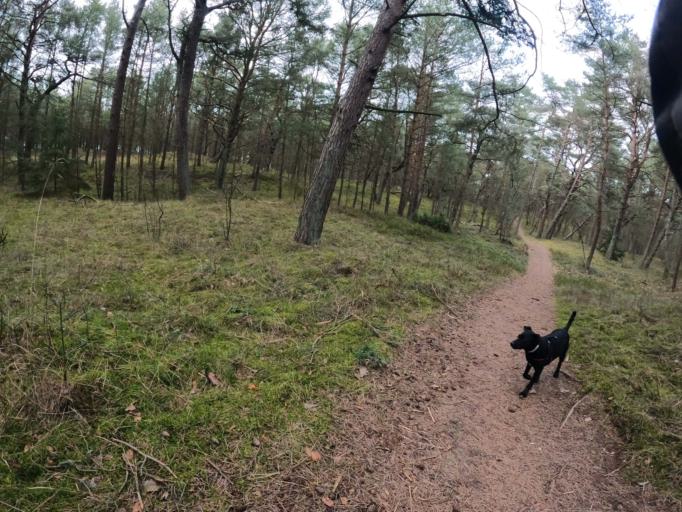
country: PL
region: West Pomeranian Voivodeship
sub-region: Powiat gryficki
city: Mrzezyno
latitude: 54.1358
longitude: 15.2577
